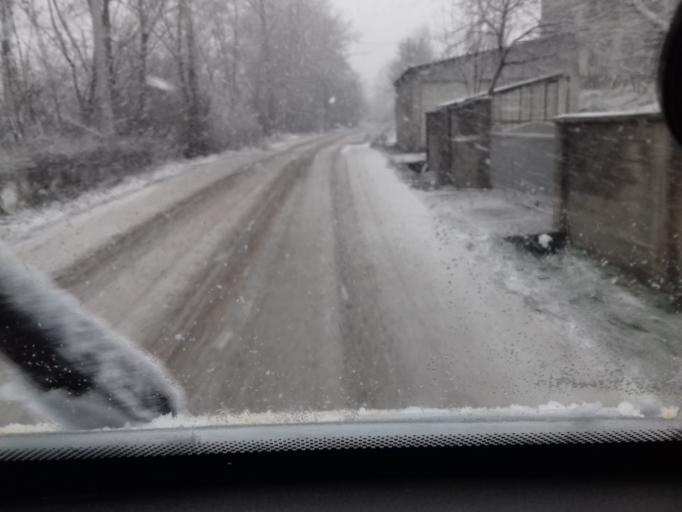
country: BA
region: Federation of Bosnia and Herzegovina
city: Lokvine
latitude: 44.2240
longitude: 17.8580
